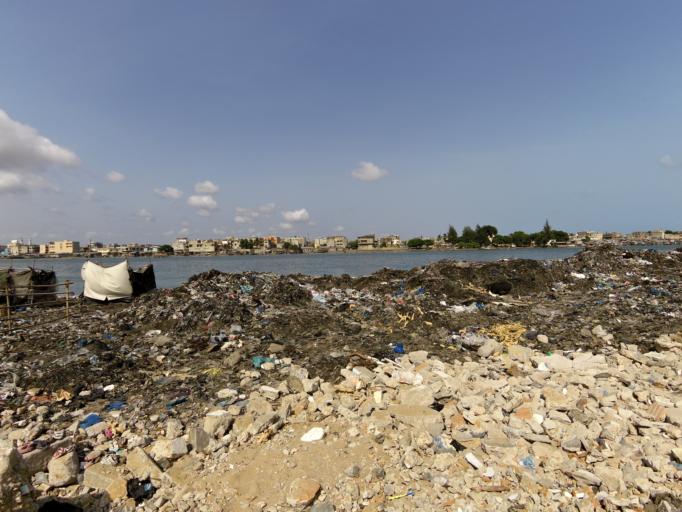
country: BJ
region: Littoral
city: Cotonou
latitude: 6.3659
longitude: 2.4371
